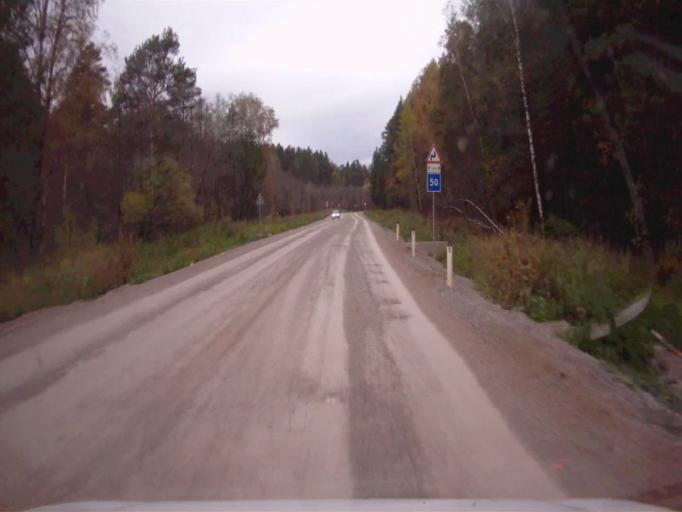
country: RU
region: Chelyabinsk
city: Nyazepetrovsk
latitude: 56.0442
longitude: 59.5054
